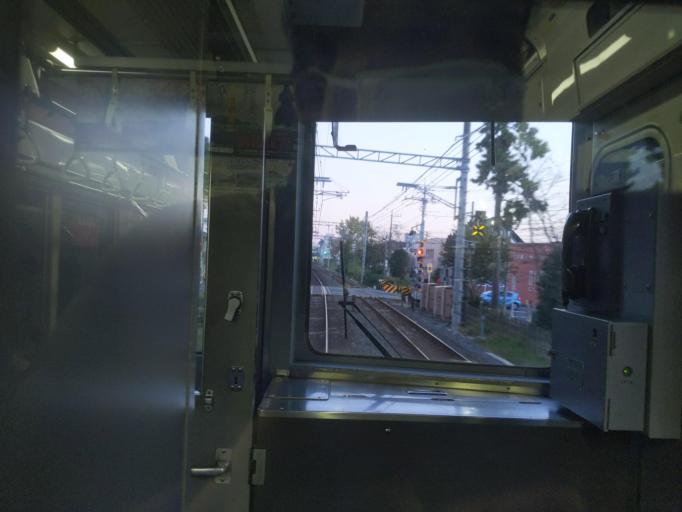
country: JP
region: Chiba
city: Nagareyama
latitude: 35.9002
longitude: 139.9088
